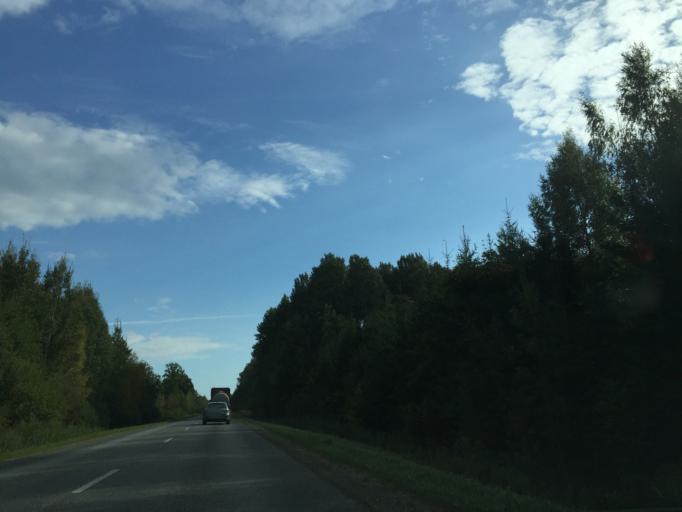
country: LV
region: Limbazu Rajons
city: Limbazi
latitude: 57.5188
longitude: 24.5394
